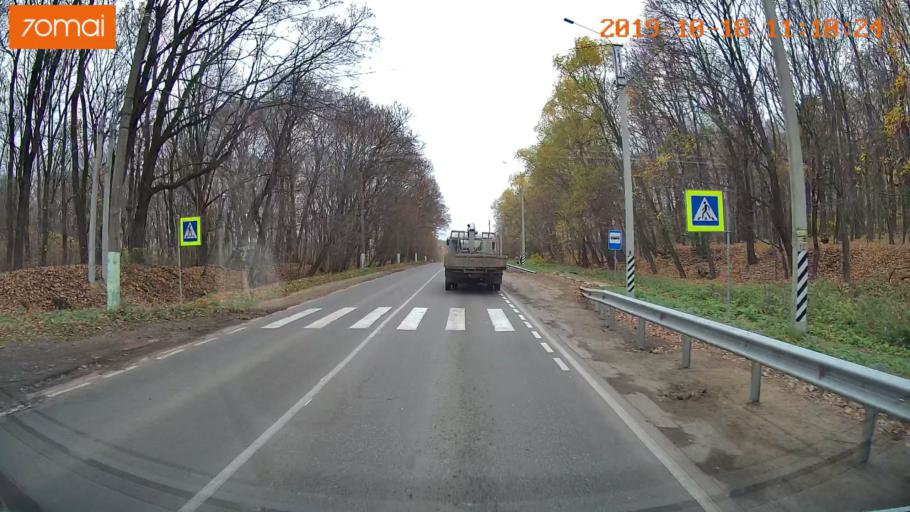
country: RU
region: Tula
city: Kimovsk
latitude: 53.9552
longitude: 38.5390
